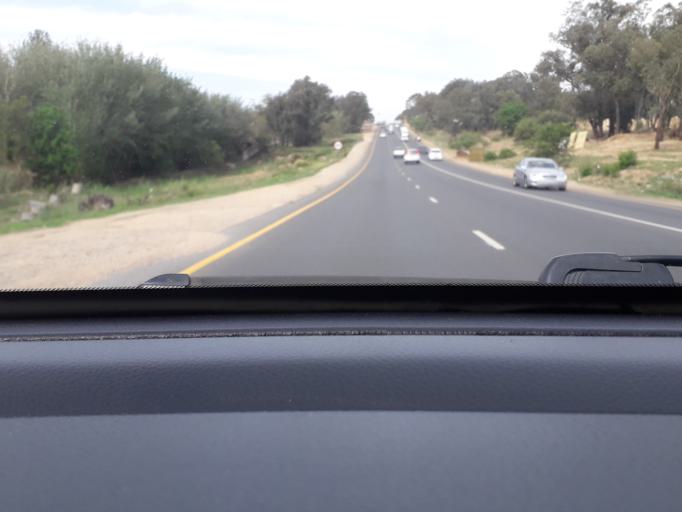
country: ZA
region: Gauteng
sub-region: City of Johannesburg Metropolitan Municipality
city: Diepsloot
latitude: -26.0284
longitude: 27.9790
